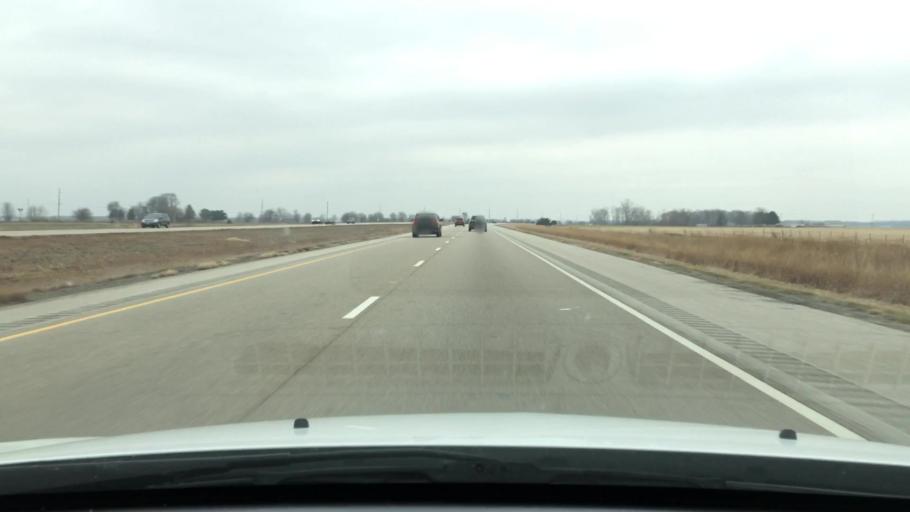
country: US
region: Illinois
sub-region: Logan County
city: Lincoln
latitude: 40.1929
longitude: -89.3060
